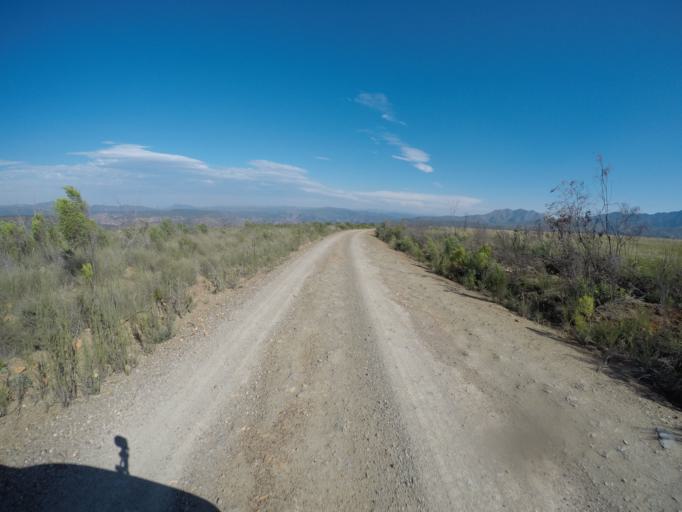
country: ZA
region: Eastern Cape
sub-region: Cacadu District Municipality
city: Kareedouw
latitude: -33.6342
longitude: 24.4774
